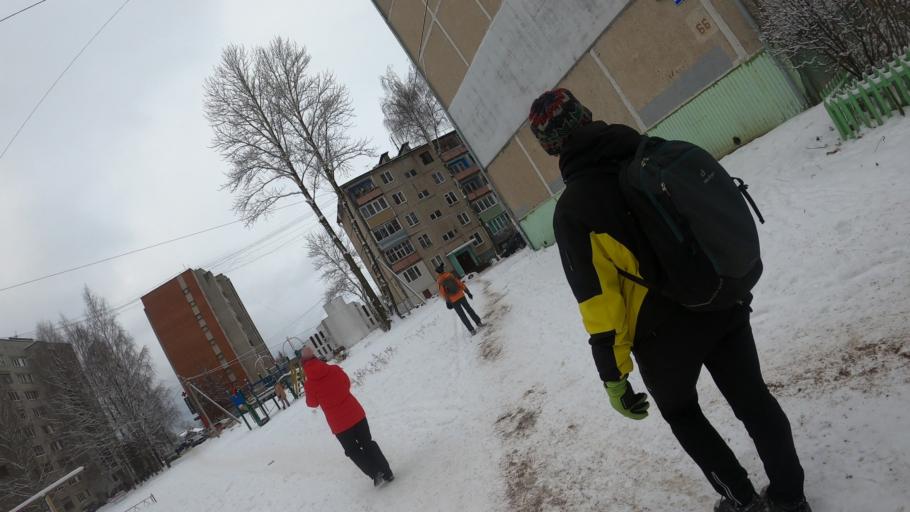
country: RU
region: Jaroslavl
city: Pereslavl'-Zalesskiy
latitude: 56.7507
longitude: 38.8754
